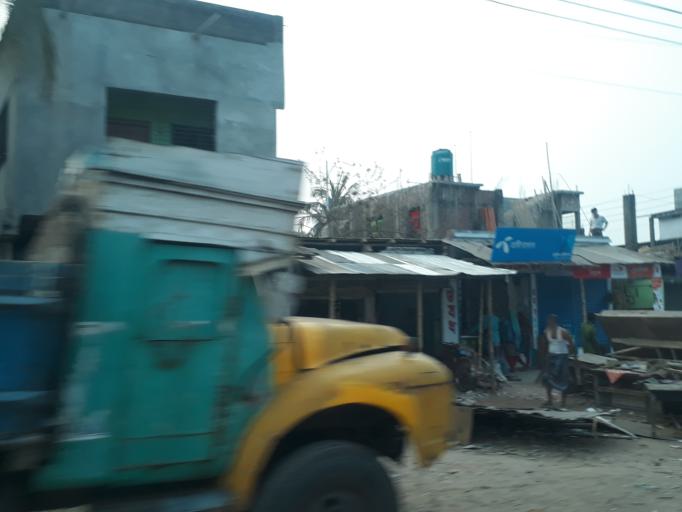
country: BD
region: Khulna
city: Bhatpara Abhaynagar
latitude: 22.9568
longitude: 89.4804
